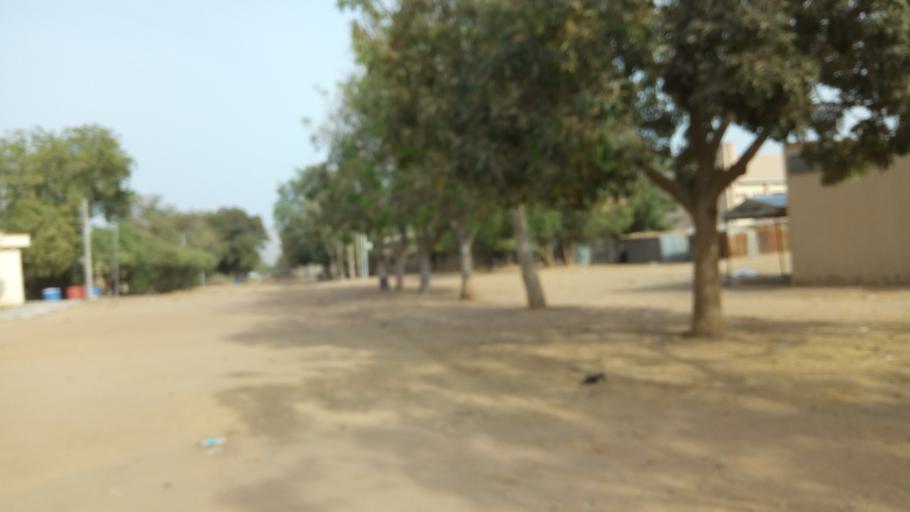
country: NG
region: Gombe
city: Gombe
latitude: 10.3077
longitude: 11.1727
